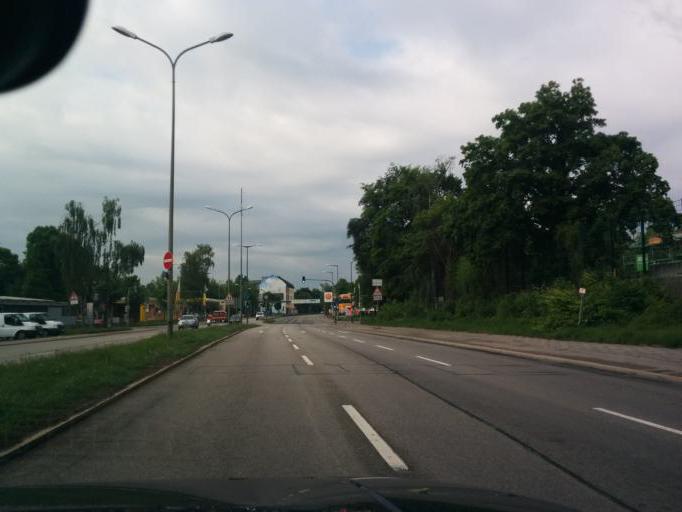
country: DE
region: Bavaria
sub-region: Upper Bavaria
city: Bogenhausen
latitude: 48.1162
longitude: 11.6181
